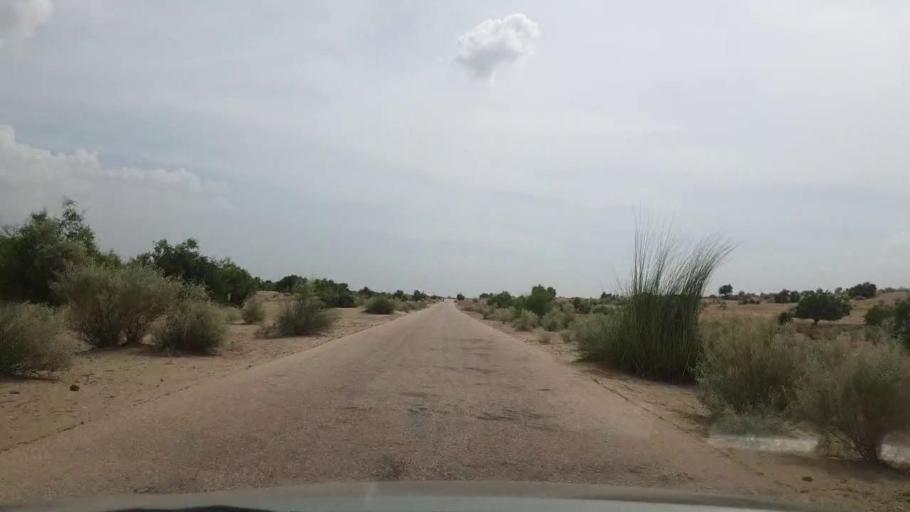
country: PK
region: Sindh
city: Kot Diji
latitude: 27.1530
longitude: 69.0340
